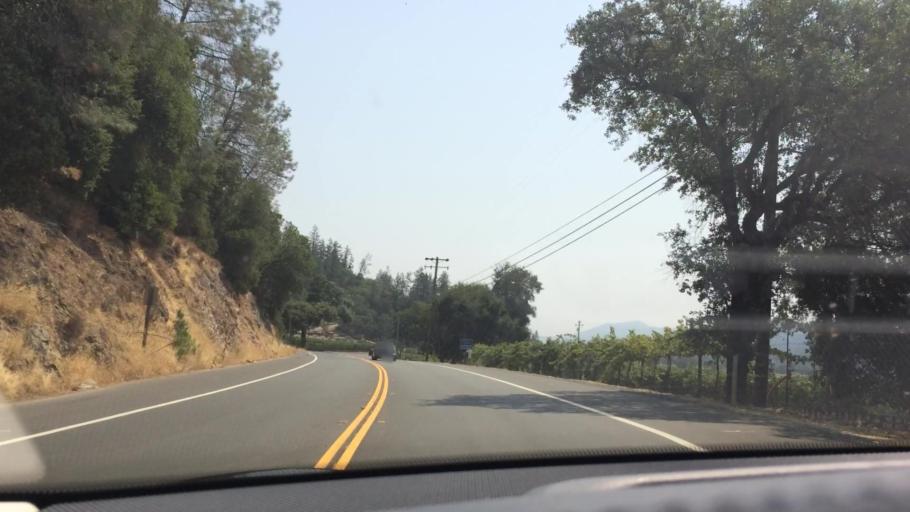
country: US
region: California
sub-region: Napa County
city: Calistoga
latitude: 38.5721
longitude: -122.5180
